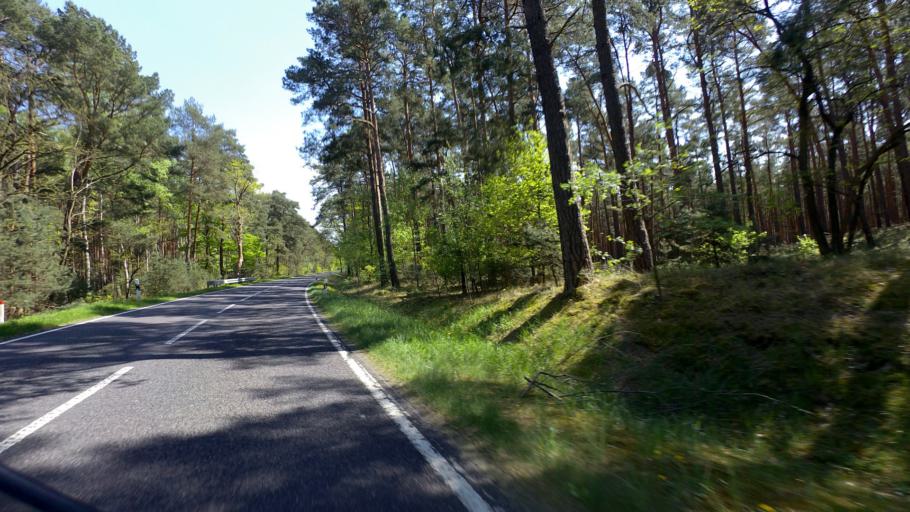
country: DE
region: Brandenburg
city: Munchehofe
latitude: 52.1022
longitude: 13.8086
